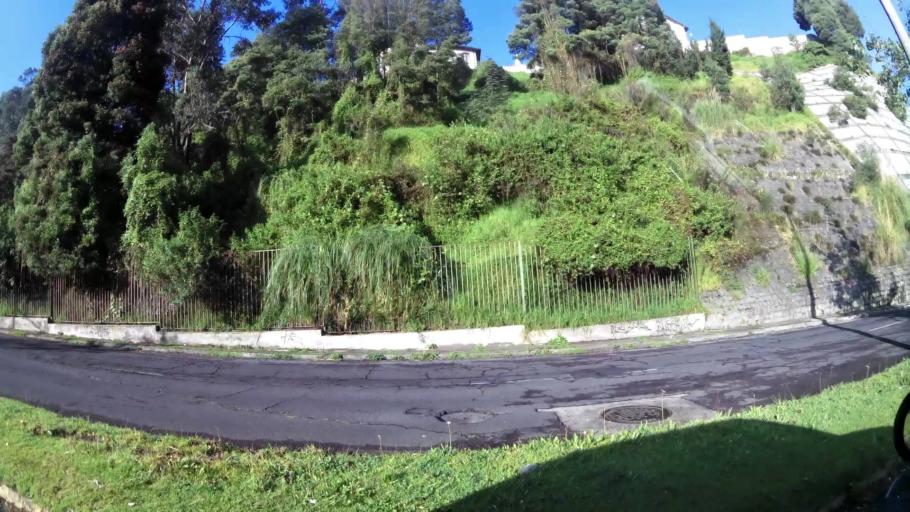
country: EC
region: Pichincha
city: Quito
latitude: -0.2340
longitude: -78.5128
